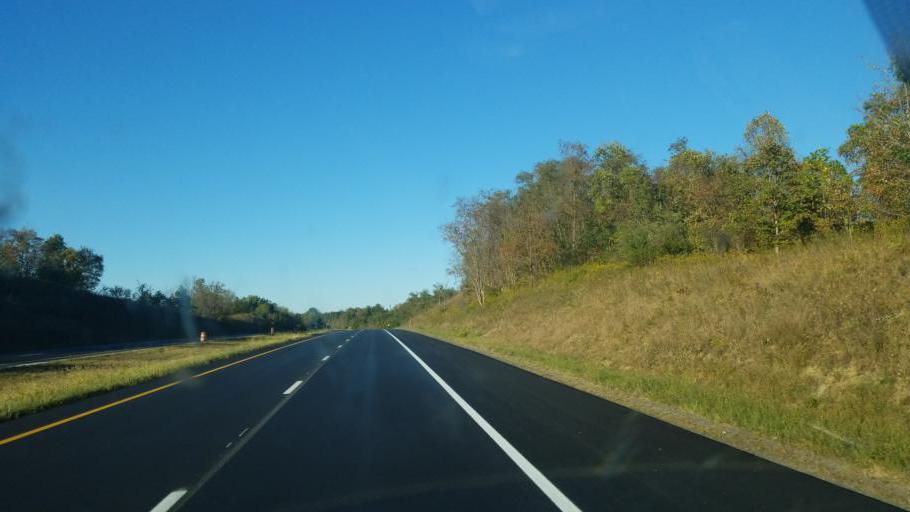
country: US
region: Ohio
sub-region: Guernsey County
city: Cambridge
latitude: 40.0825
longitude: -81.5620
